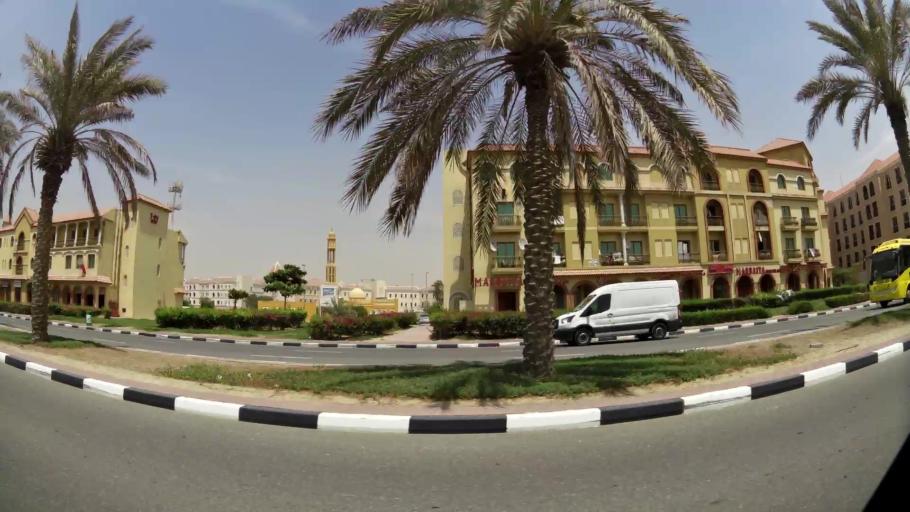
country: AE
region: Ash Shariqah
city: Sharjah
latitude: 25.1670
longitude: 55.3974
